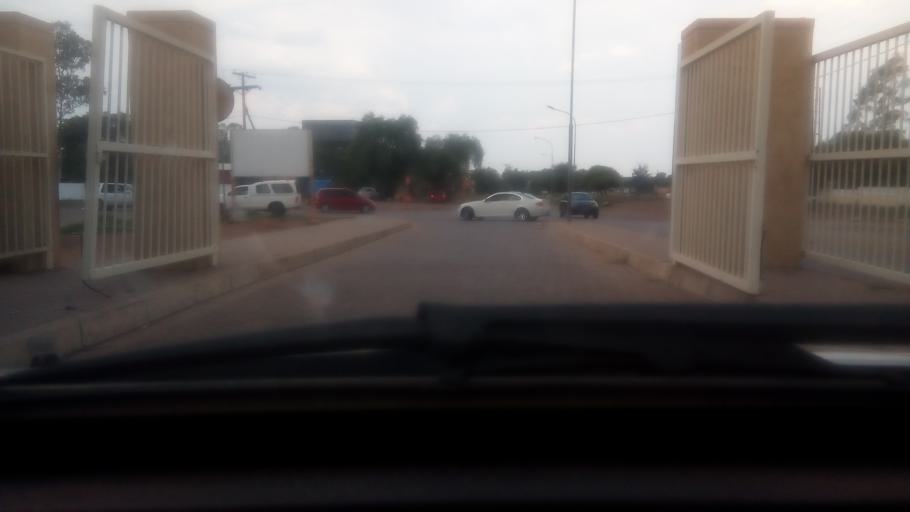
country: BW
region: Kweneng
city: Molepolole
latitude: -24.4118
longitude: 25.4881
